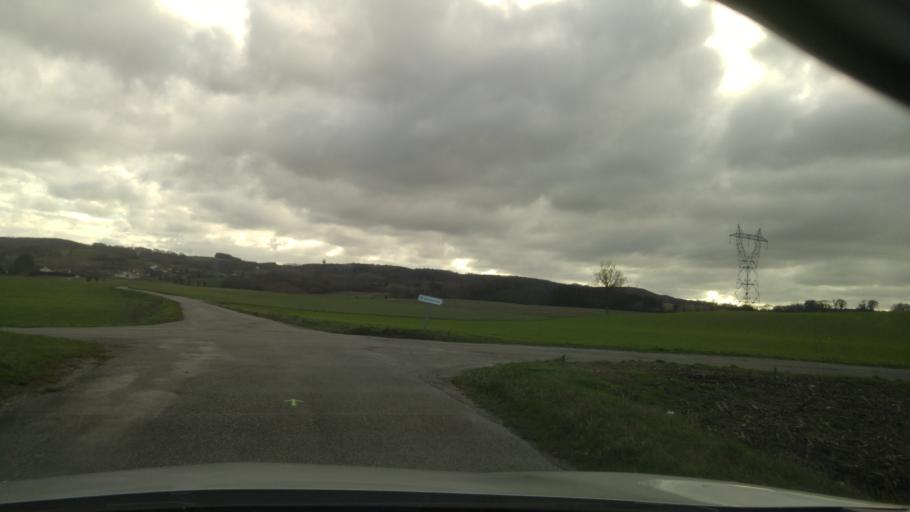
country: FR
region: Rhone-Alpes
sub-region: Departement de l'Isere
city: Roche
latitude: 45.5778
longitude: 5.1740
